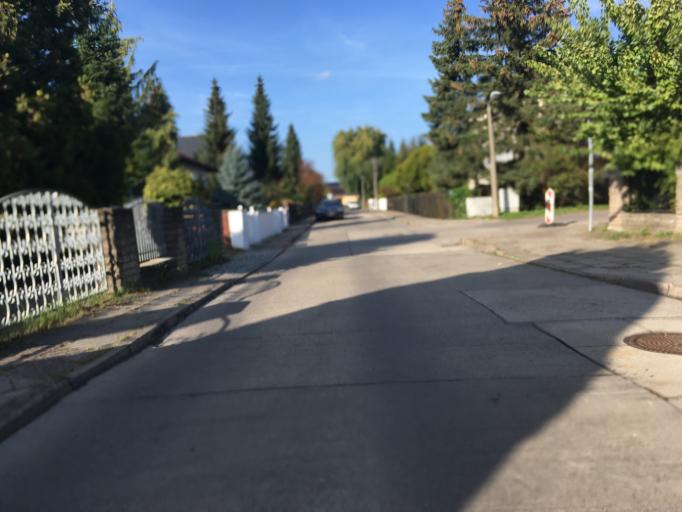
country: DE
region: Berlin
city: Niederschonhausen
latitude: 52.5900
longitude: 13.3907
